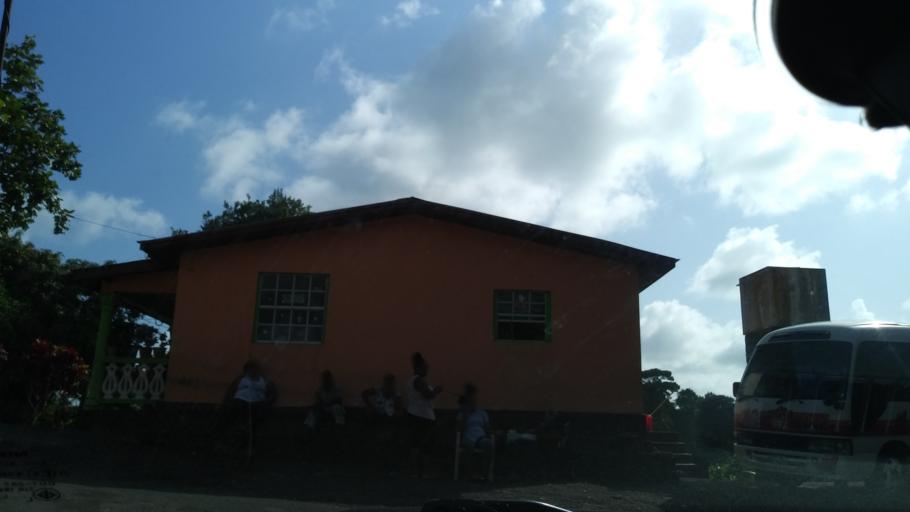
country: VC
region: Charlotte
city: Byera Village
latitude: 13.2400
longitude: -61.1326
